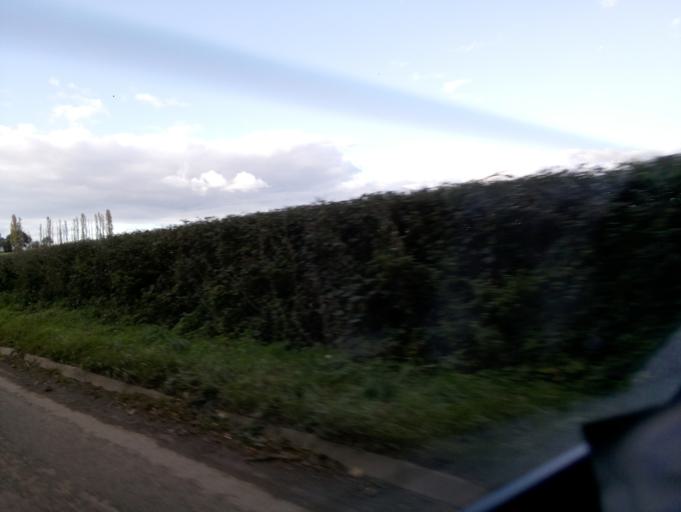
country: GB
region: England
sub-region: Herefordshire
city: Withington
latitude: 52.0617
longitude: -2.6253
